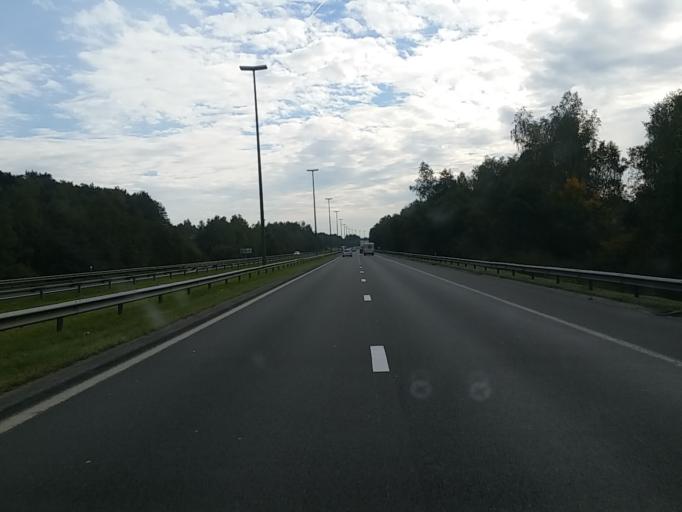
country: BE
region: Wallonia
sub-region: Province du Luxembourg
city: Attert
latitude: 49.6908
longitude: 5.7292
